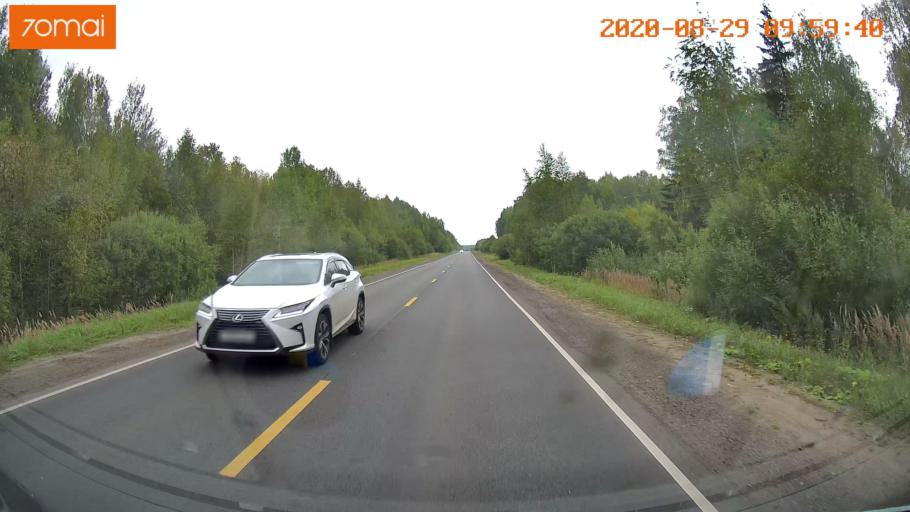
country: RU
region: Ivanovo
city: Zarechnyy
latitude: 57.4107
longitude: 42.3722
